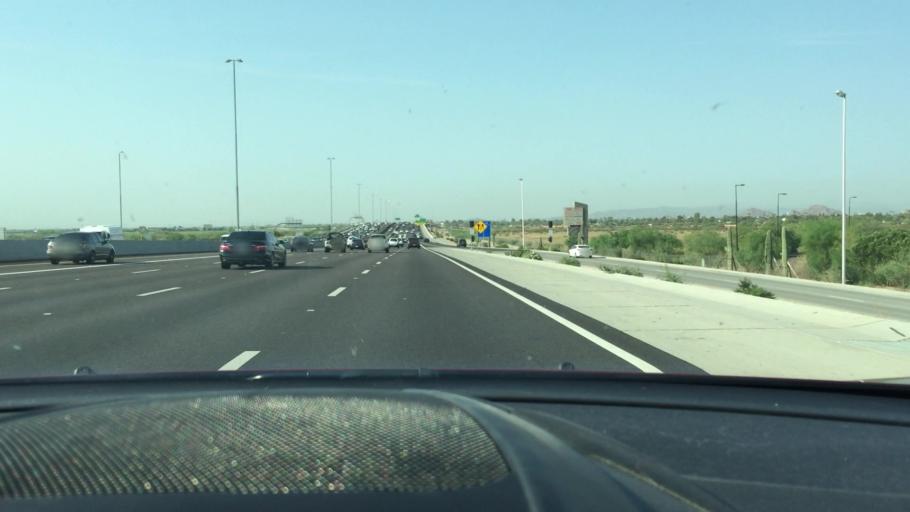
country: US
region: Arizona
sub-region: Maricopa County
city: Scottsdale
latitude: 33.5367
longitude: -111.8823
